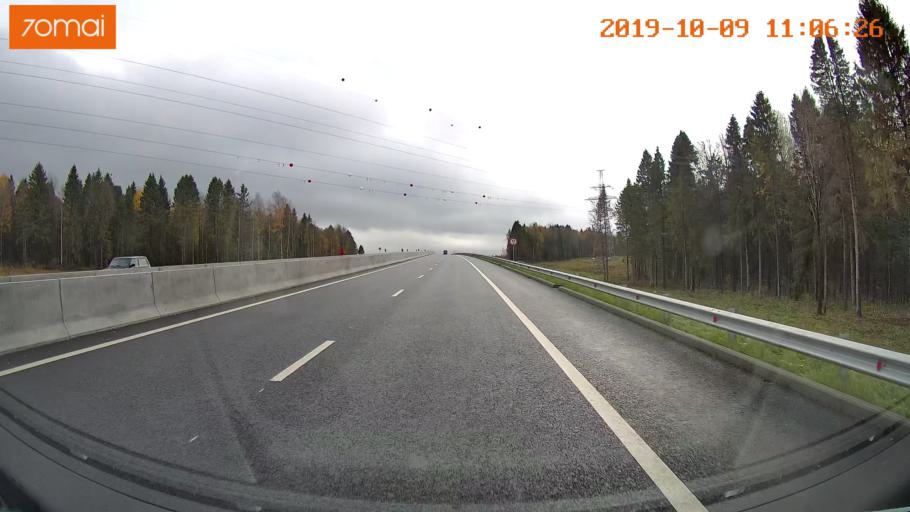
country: RU
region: Vologda
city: Vologda
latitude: 59.1865
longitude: 39.7605
